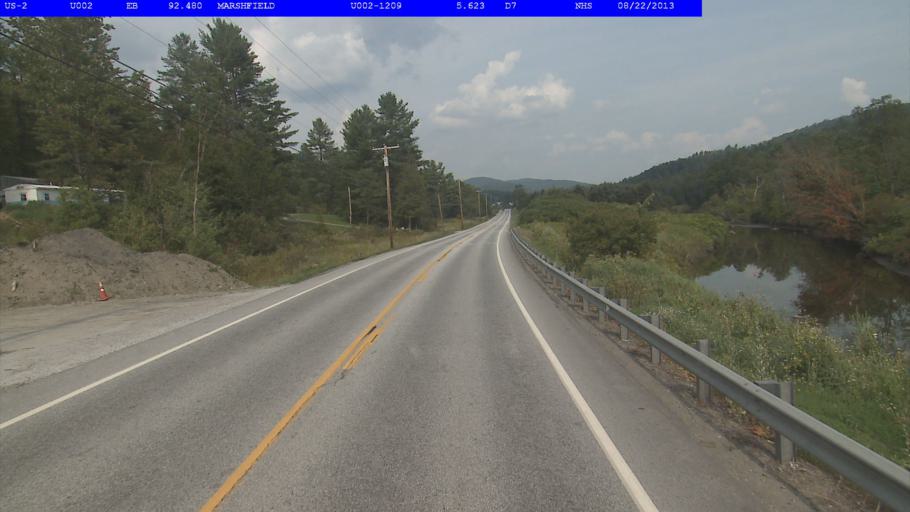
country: US
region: Vermont
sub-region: Caledonia County
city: Hardwick
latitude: 44.3439
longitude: -72.3675
